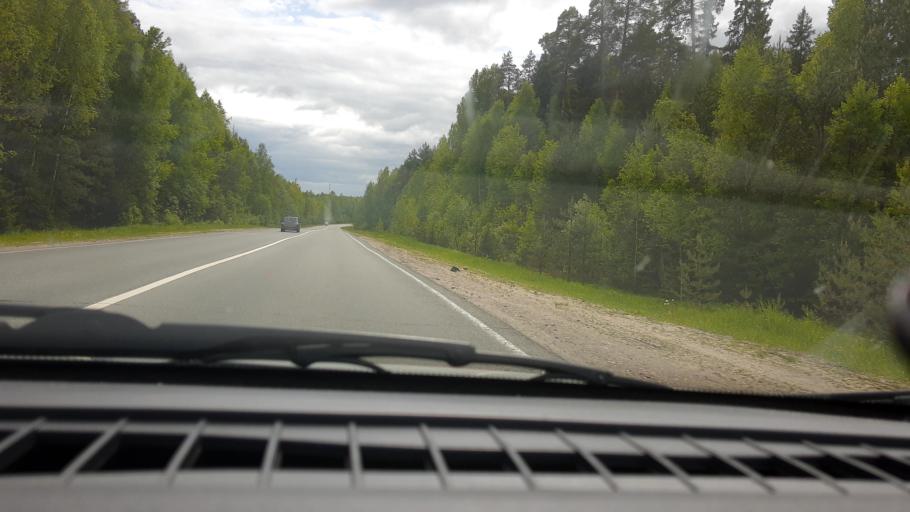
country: RU
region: Nizjnij Novgorod
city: Semenov
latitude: 56.8008
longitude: 44.4605
